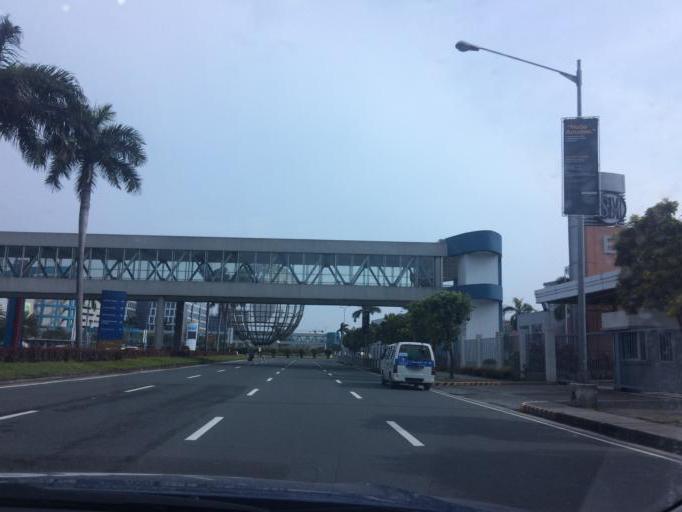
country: PH
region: Metro Manila
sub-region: Makati City
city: Makati City
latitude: 14.5335
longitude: 120.9845
